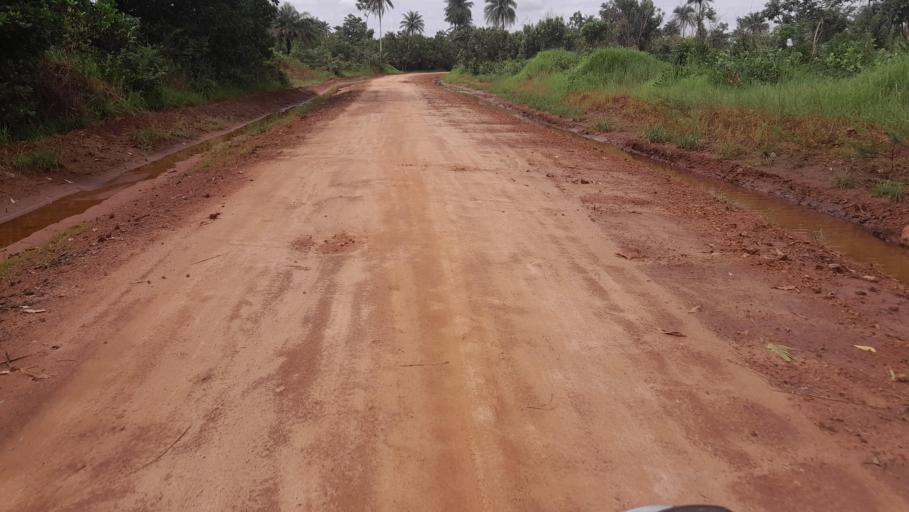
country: GN
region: Boke
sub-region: Boffa
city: Boffa
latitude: 10.0713
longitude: -13.8679
